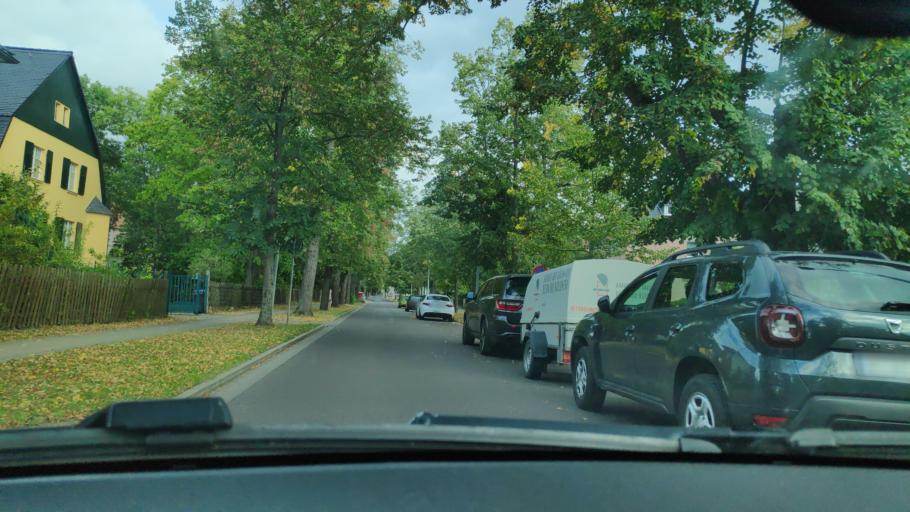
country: DE
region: Saxony-Anhalt
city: Biederitz
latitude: 52.1538
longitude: 11.7107
